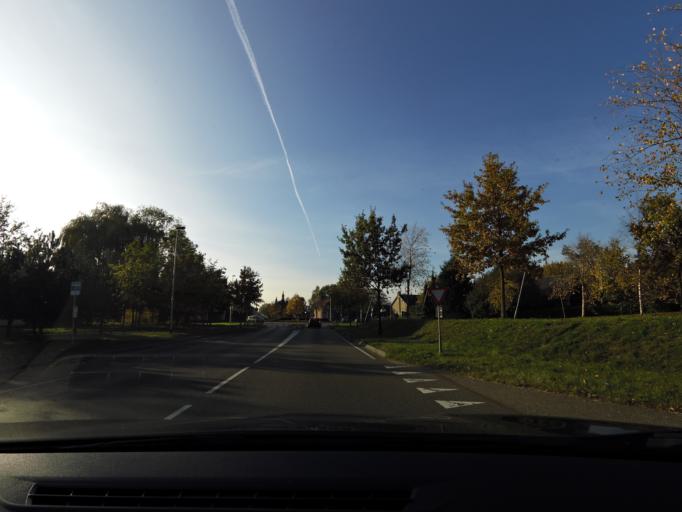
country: NL
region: North Brabant
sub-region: Gemeente Breda
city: Breda
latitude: 51.6049
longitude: 4.7191
